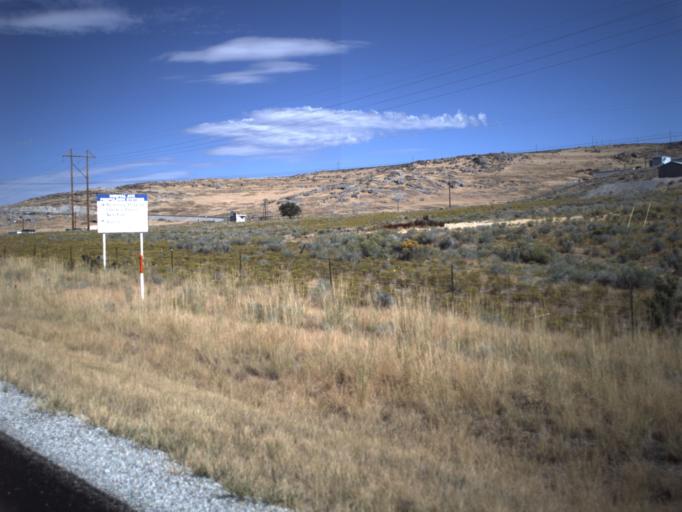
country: US
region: Utah
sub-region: Box Elder County
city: Tremonton
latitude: 41.6343
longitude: -112.4217
